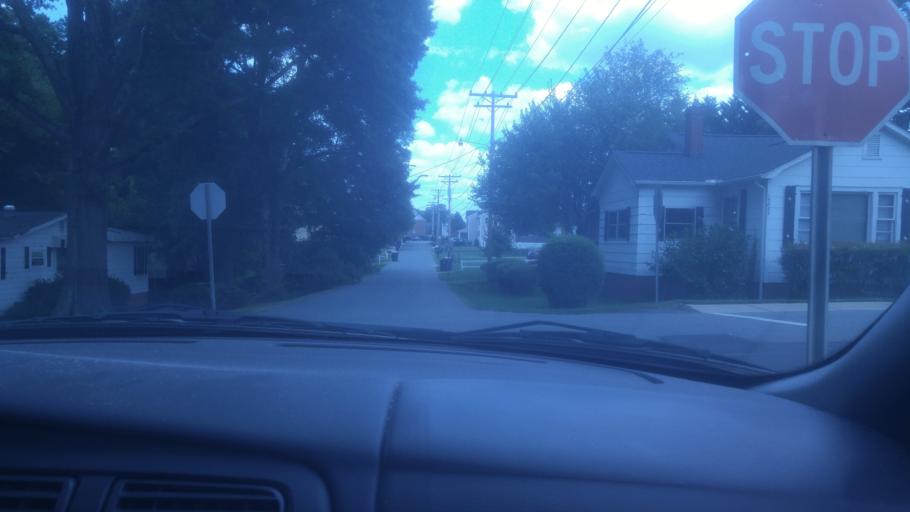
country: US
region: North Carolina
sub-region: Mecklenburg County
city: Cornelius
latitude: 35.4841
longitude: -80.8623
